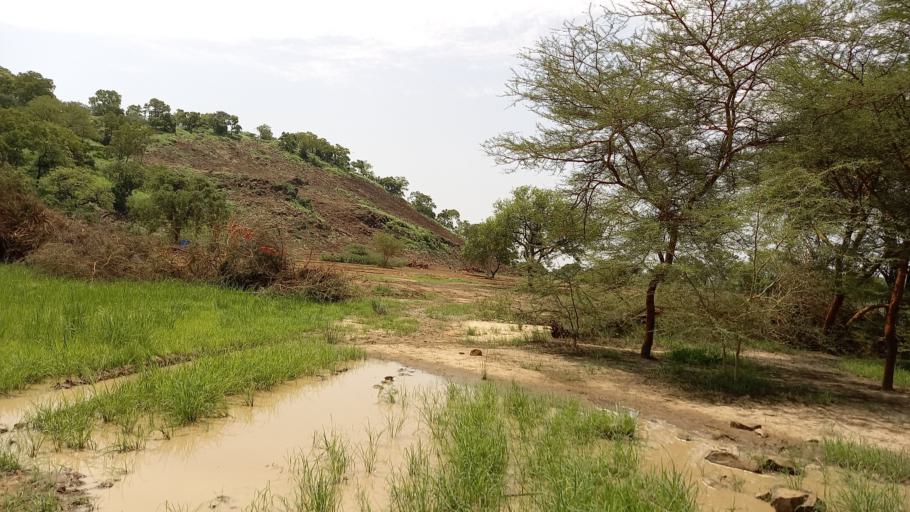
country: ET
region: Gambela
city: Gambela
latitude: 8.2853
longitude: 34.2117
